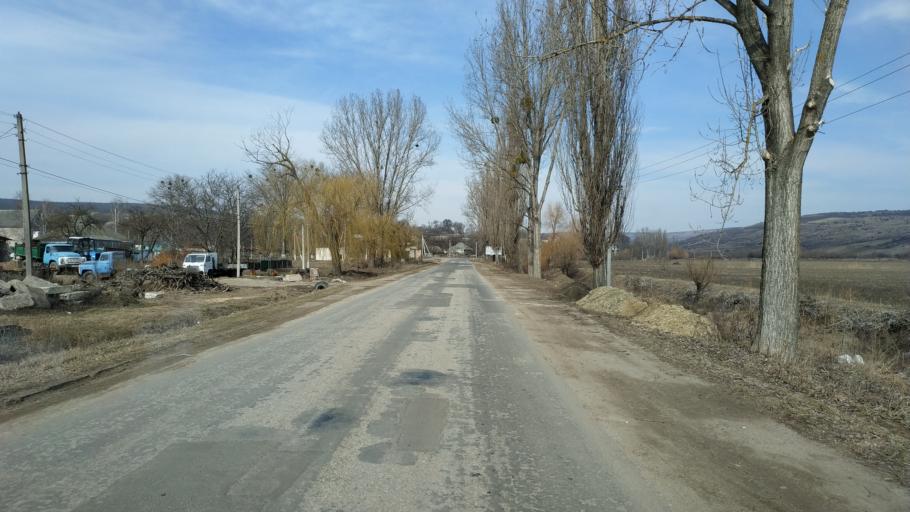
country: MD
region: Nisporeni
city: Nisporeni
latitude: 47.1475
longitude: 28.1090
